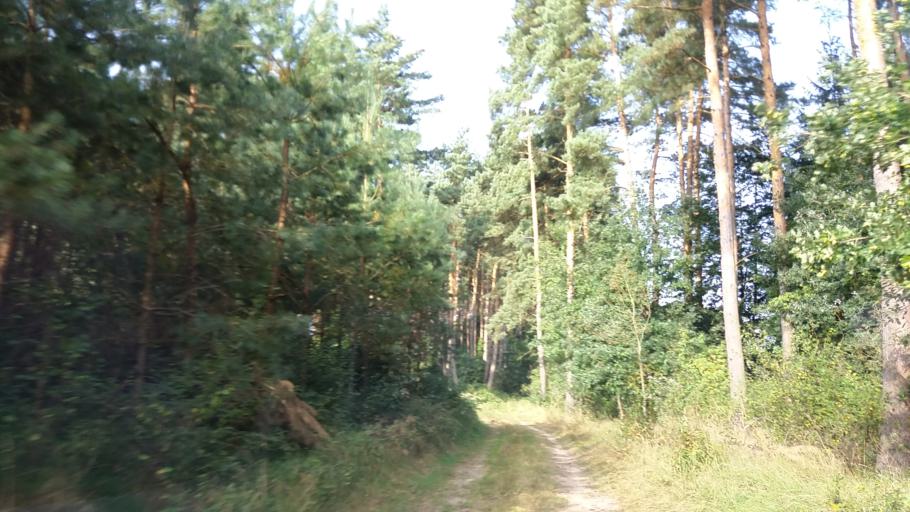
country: PL
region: West Pomeranian Voivodeship
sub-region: Powiat stargardzki
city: Suchan
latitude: 53.2436
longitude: 15.3811
